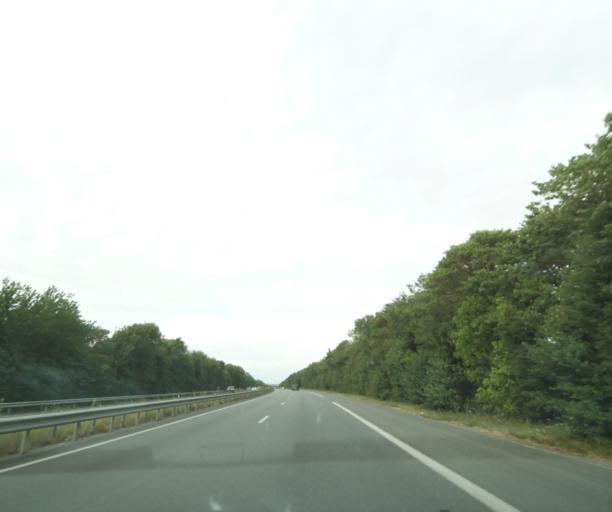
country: FR
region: Poitou-Charentes
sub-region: Departement de la Charente-Maritime
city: Dompierre-sur-Mer
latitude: 46.1850
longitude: -1.0782
